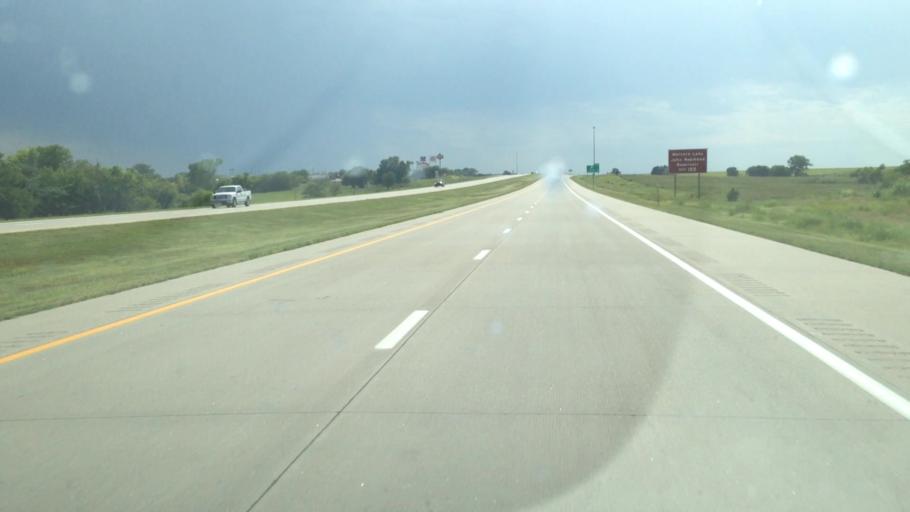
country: US
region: Kansas
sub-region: Osage County
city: Lyndon
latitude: 38.4321
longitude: -95.7180
